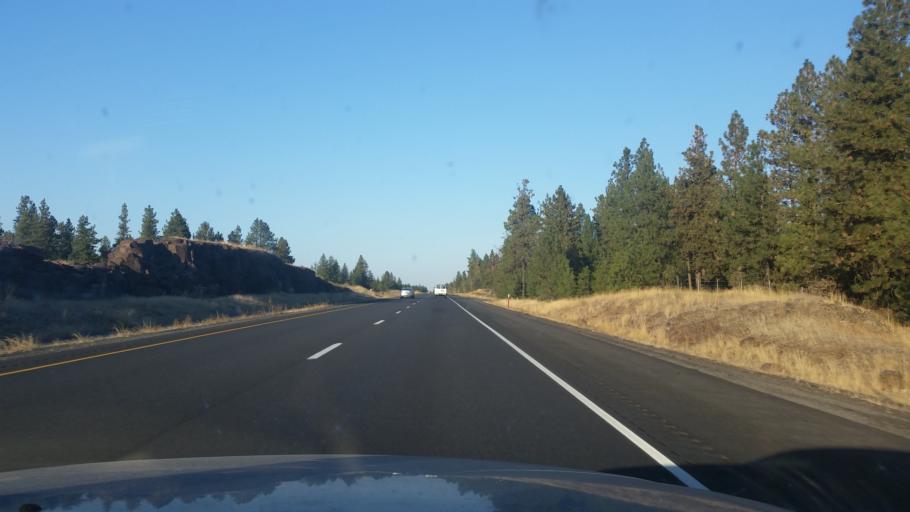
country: US
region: Washington
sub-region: Spokane County
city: Medical Lake
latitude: 47.4619
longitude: -117.7528
